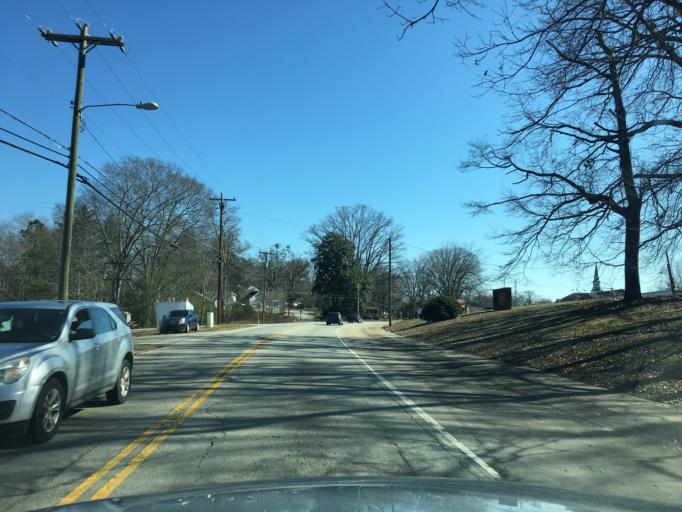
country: US
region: South Carolina
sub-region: Pickens County
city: Liberty
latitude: 34.7858
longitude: -82.6889
